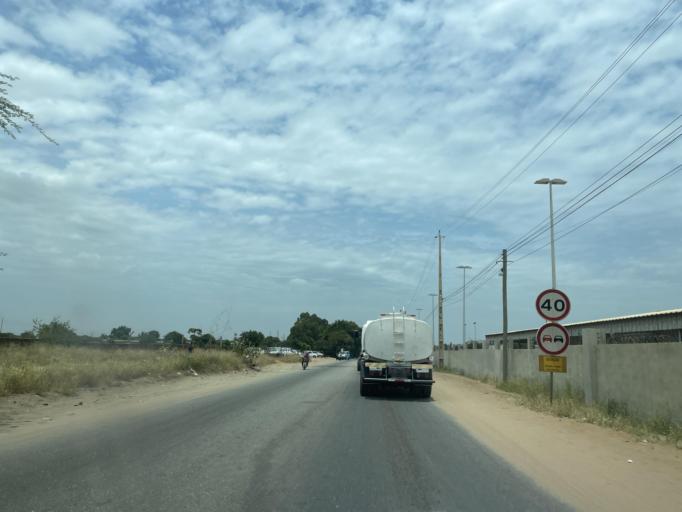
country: AO
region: Luanda
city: Luanda
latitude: -8.9379
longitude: 13.3894
